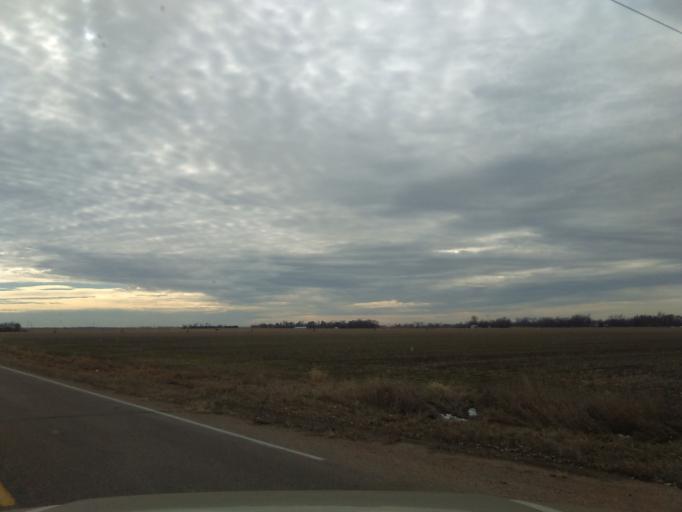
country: US
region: Nebraska
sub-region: Buffalo County
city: Gibbon
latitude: 40.6549
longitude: -98.8473
